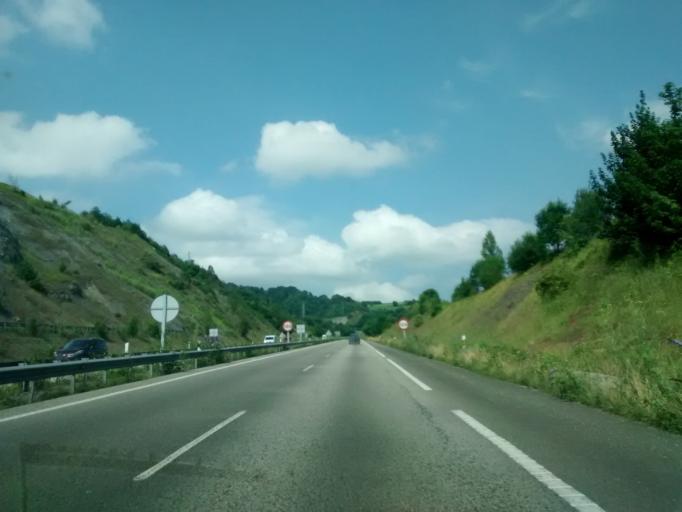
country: ES
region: Asturias
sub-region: Province of Asturias
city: Sama
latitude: 43.3330
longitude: -5.7187
